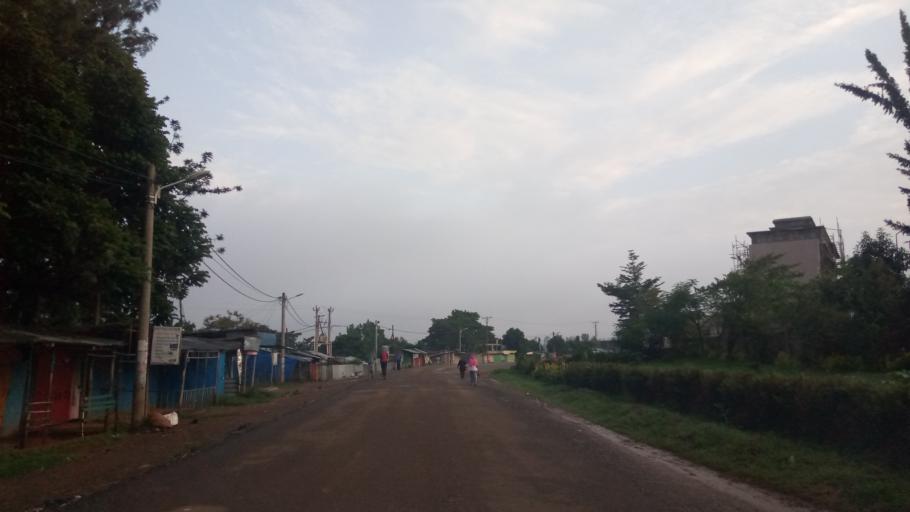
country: ET
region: Oromiya
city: Jima
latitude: 7.6778
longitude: 36.8512
